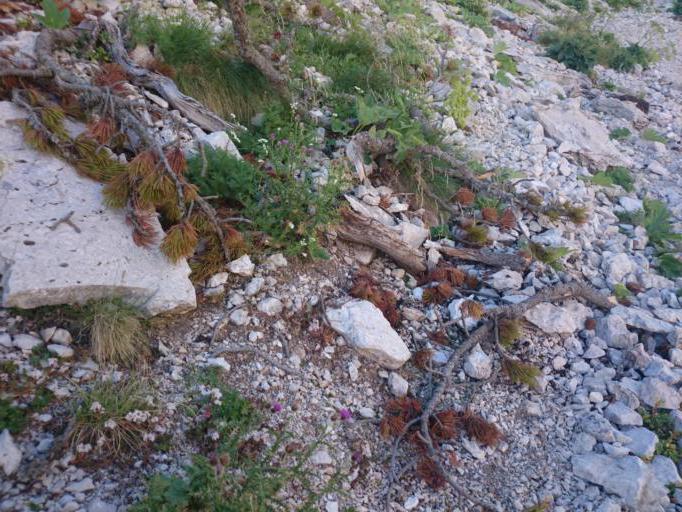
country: AL
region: Elbasan
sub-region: Rrethi i Gramshit
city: Kushove
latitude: 40.7157
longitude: 20.1484
